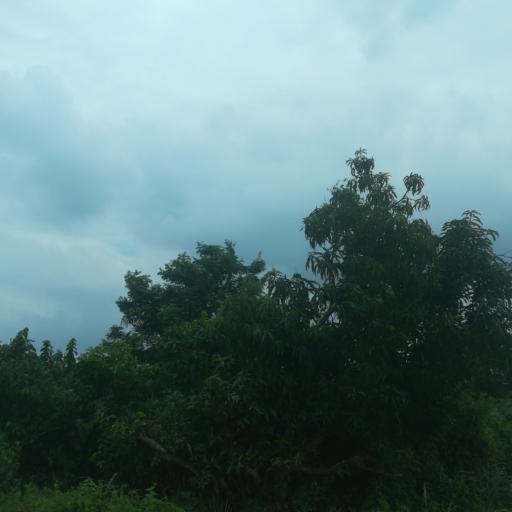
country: NG
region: Lagos
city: Ejirin
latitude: 6.6438
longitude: 3.7268
